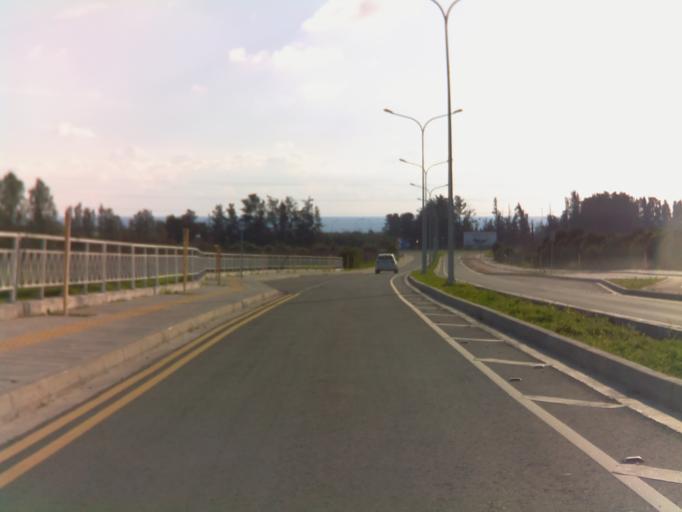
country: CY
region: Pafos
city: Paphos
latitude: 34.7377
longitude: 32.4636
